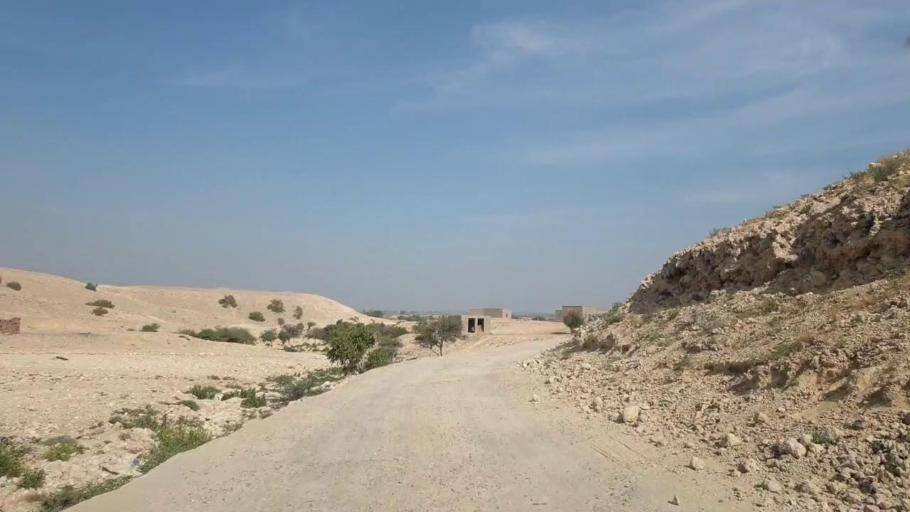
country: PK
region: Sindh
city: Hala
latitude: 25.7647
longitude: 68.2875
